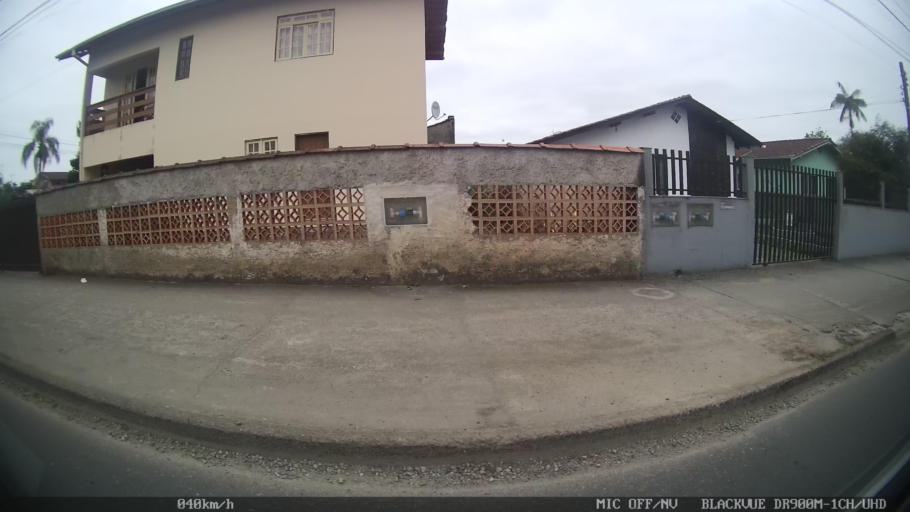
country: BR
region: Santa Catarina
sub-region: Joinville
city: Joinville
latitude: -26.3298
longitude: -48.8341
